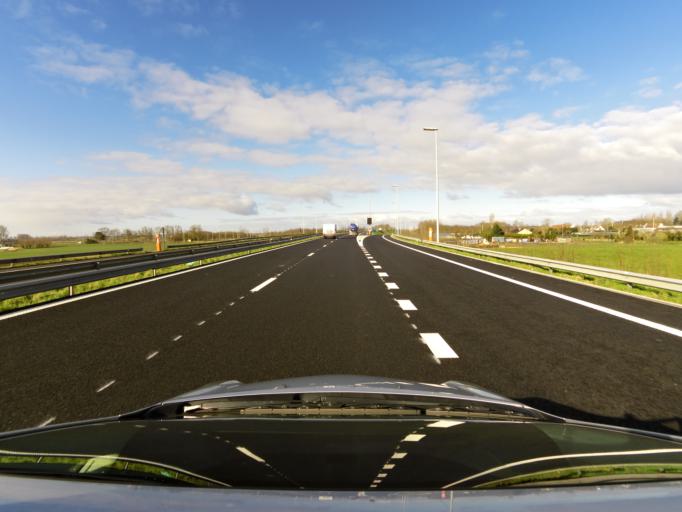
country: BE
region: Flanders
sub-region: Provincie West-Vlaanderen
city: Veurne
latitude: 51.0575
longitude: 2.6724
